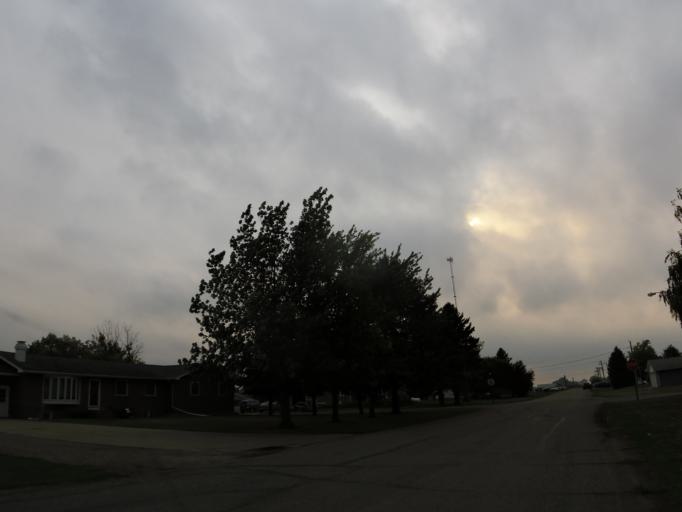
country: US
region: North Dakota
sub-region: Walsh County
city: Grafton
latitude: 48.5569
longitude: -97.1798
